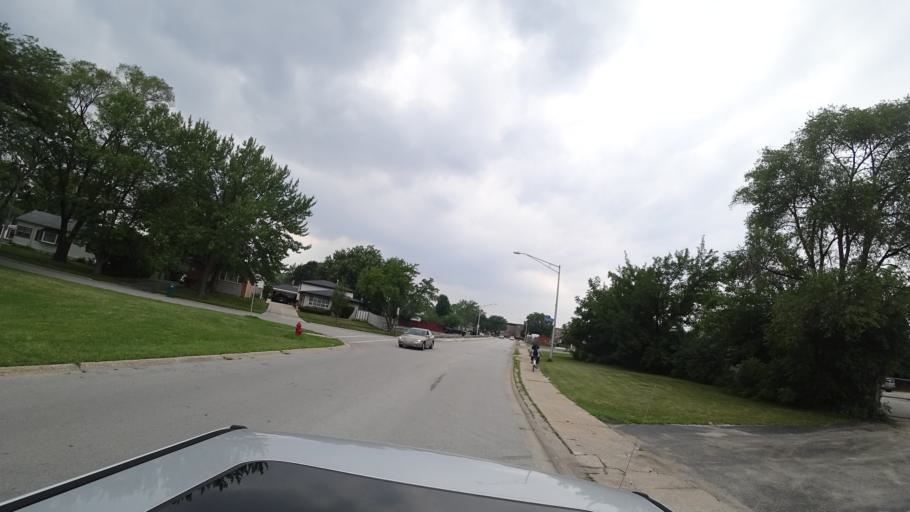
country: US
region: Illinois
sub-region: Cook County
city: Oak Lawn
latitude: 41.6950
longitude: -87.7603
